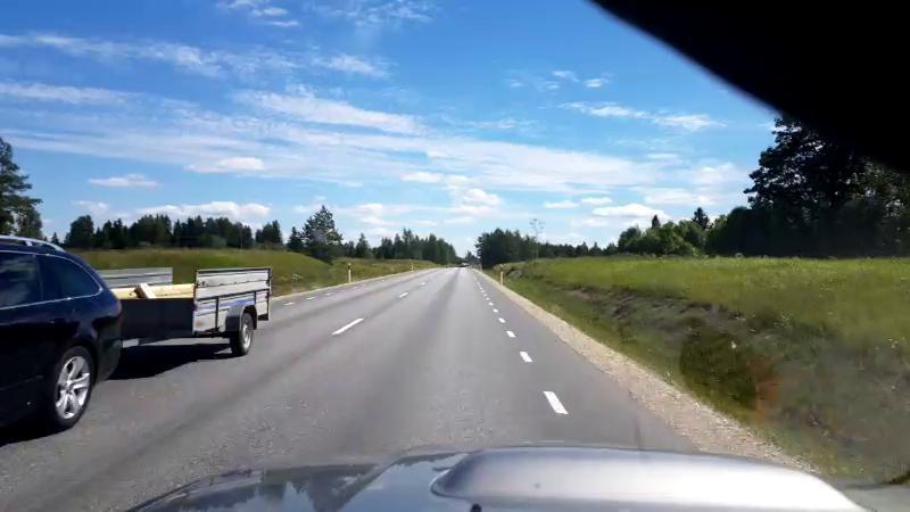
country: EE
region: Jogevamaa
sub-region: Jogeva linn
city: Jogeva
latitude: 58.7795
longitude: 26.3209
